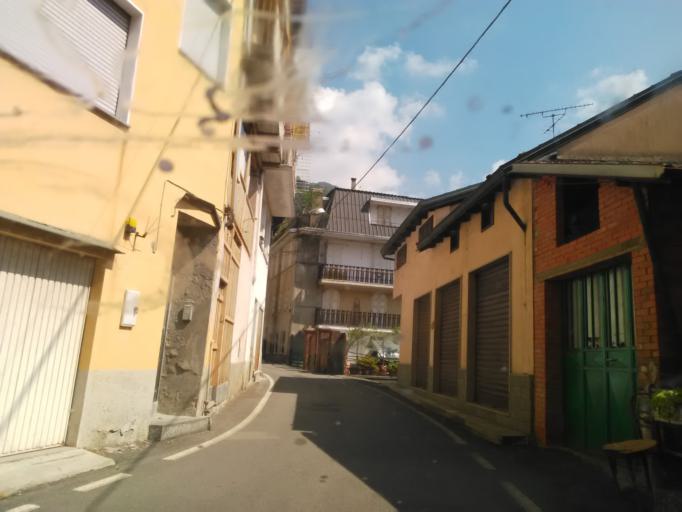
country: IT
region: Piedmont
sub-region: Provincia di Biella
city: Coggiola
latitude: 45.6902
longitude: 8.1716
